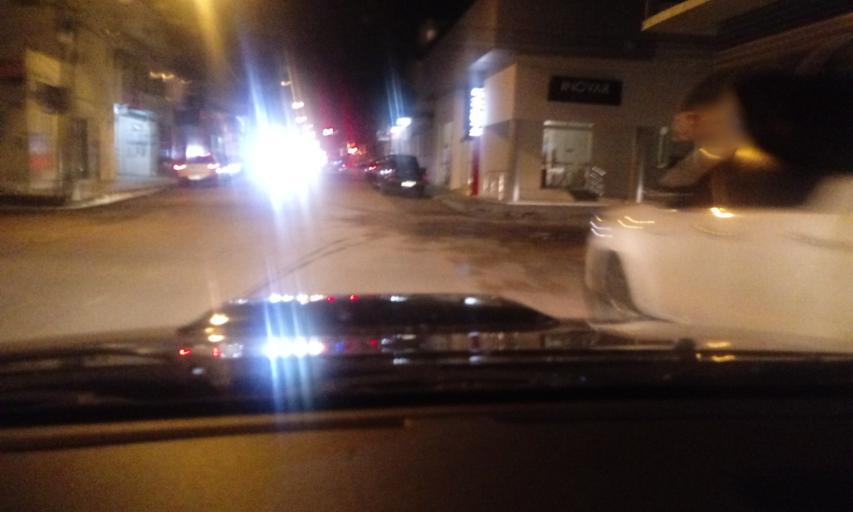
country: BR
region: Bahia
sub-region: Guanambi
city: Guanambi
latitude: -14.2178
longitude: -42.7740
